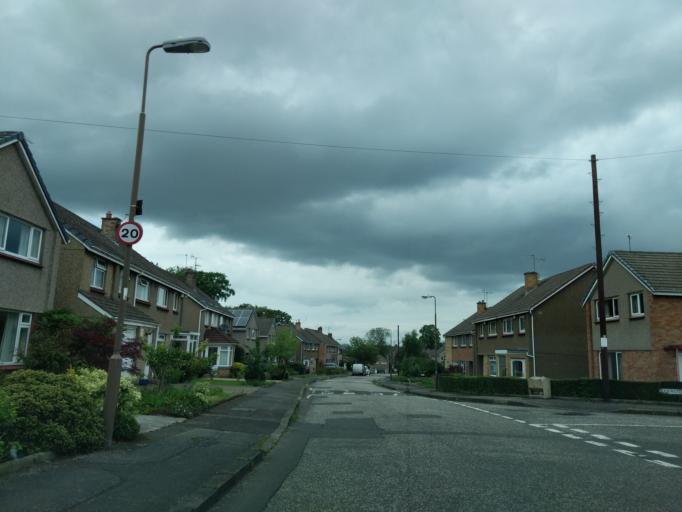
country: GB
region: Scotland
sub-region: Edinburgh
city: Colinton
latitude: 55.9493
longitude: -3.2887
